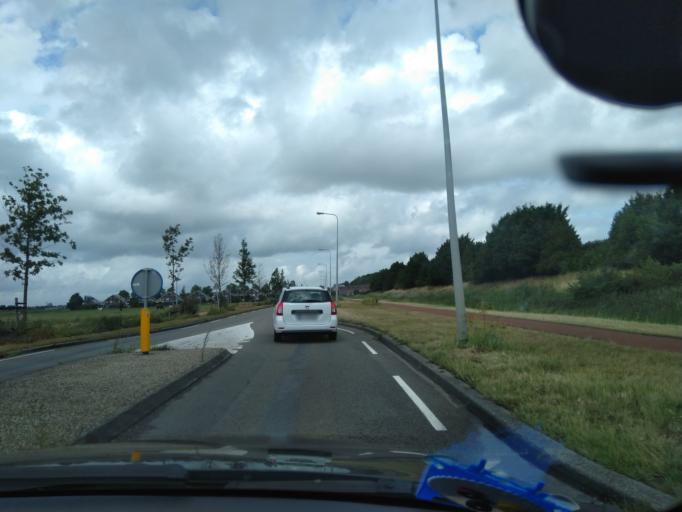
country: NL
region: Groningen
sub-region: Gemeente Groningen
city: Groningen
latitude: 53.2185
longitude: 6.5132
